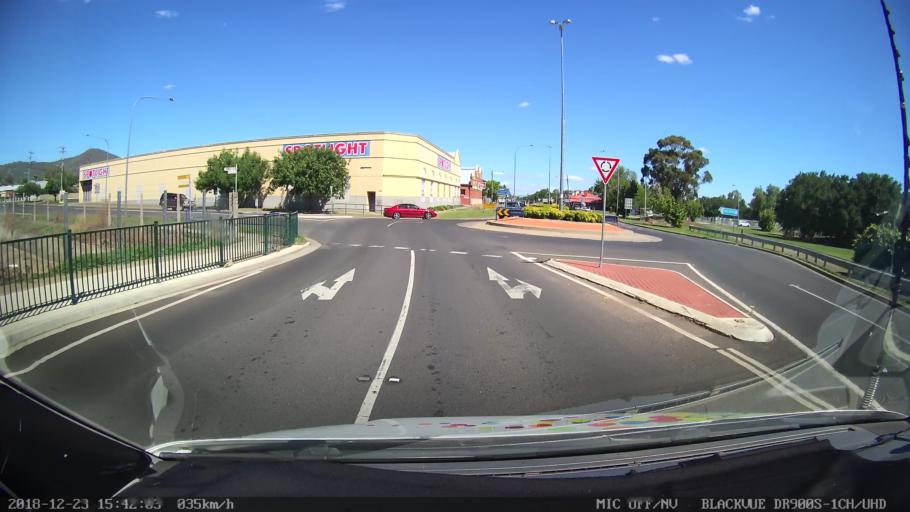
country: AU
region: New South Wales
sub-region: Tamworth Municipality
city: Tamworth
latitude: -31.0801
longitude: 150.9201
